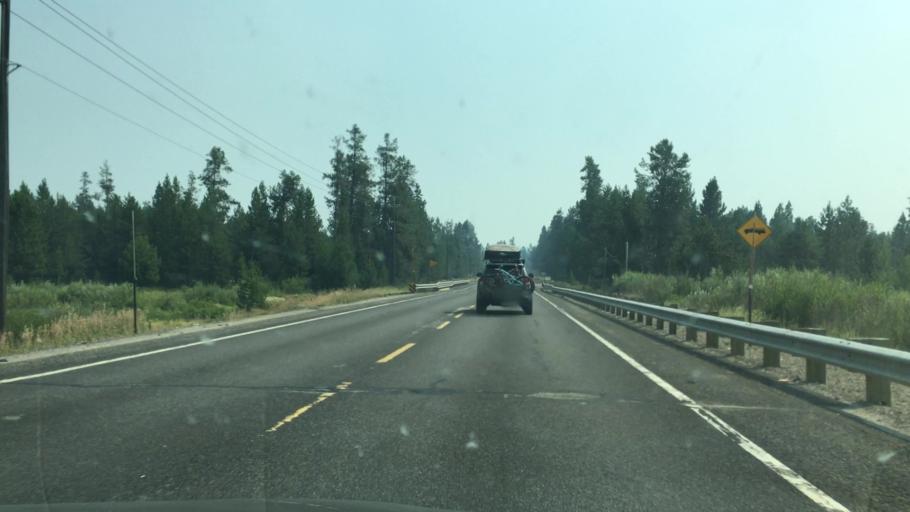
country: US
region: Idaho
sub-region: Valley County
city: Cascade
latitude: 44.4124
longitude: -115.9998
